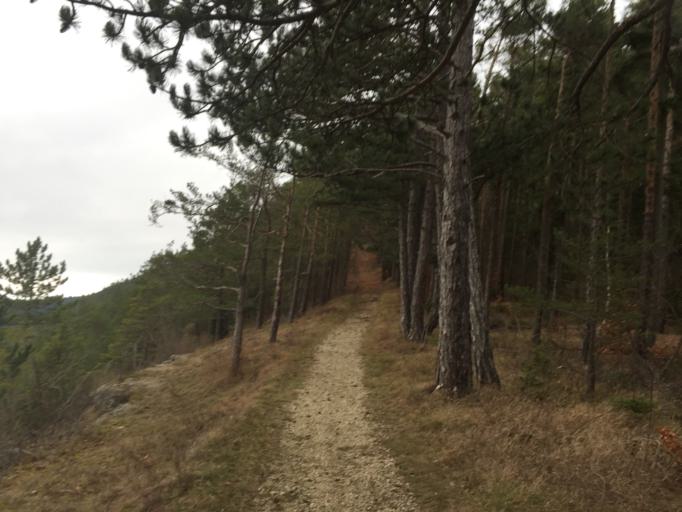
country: DE
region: Thuringia
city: Bad Blankenburg
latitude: 50.7081
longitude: 11.2328
